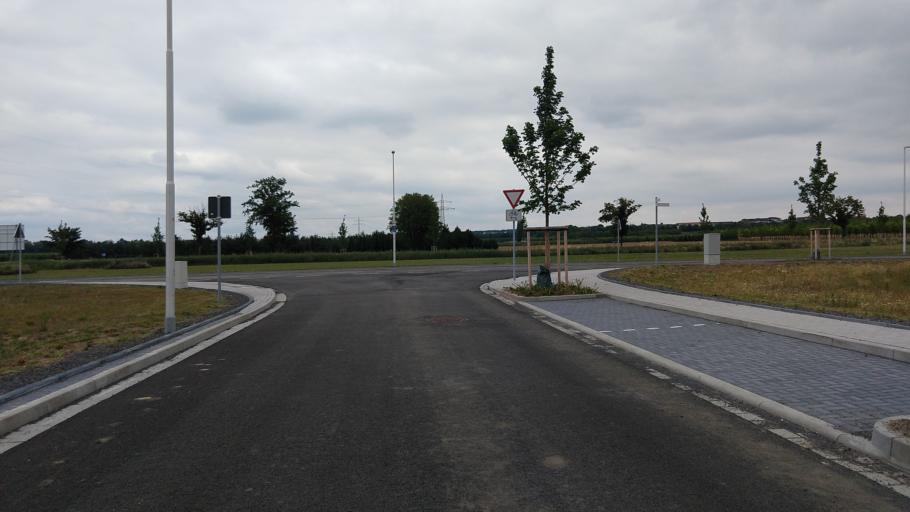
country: DE
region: North Rhine-Westphalia
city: Meckenheim
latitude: 50.6357
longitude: 7.0293
